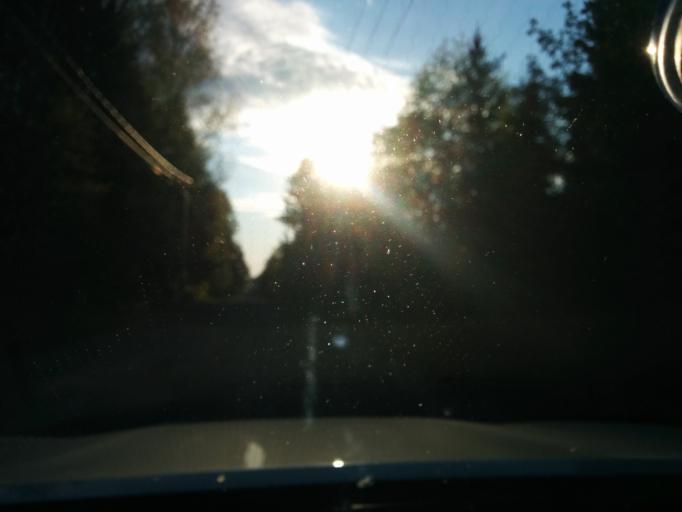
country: RU
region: Leningrad
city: Verkhniye Osel'ki
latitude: 60.2568
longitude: 30.4353
